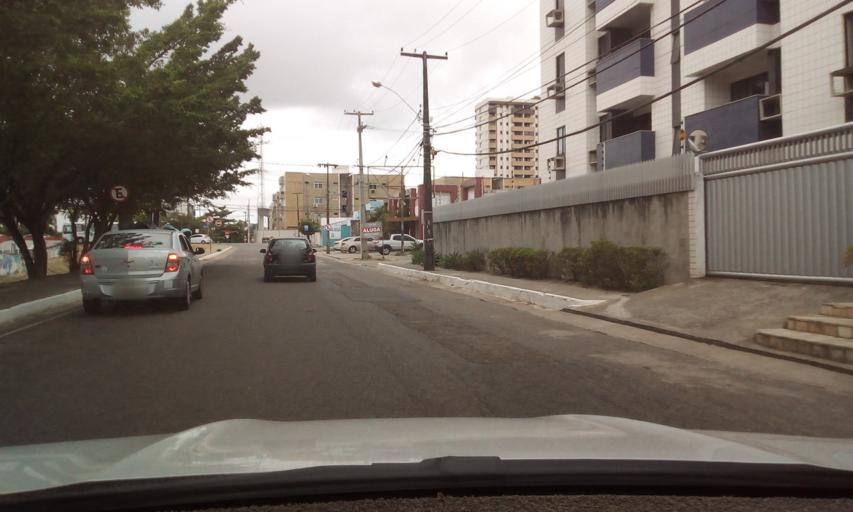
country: BR
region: Paraiba
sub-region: Joao Pessoa
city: Joao Pessoa
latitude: -7.0971
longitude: -34.8433
